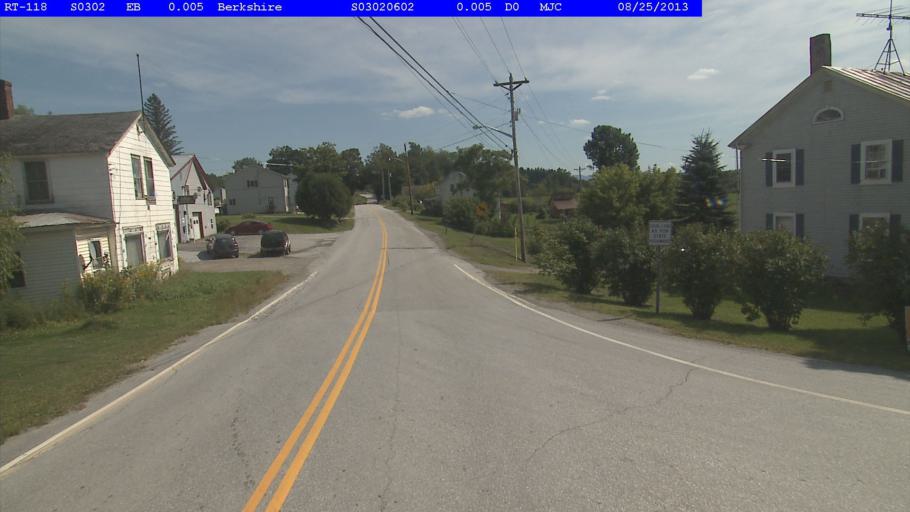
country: US
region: Vermont
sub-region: Franklin County
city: Enosburg Falls
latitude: 44.9894
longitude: -72.8130
